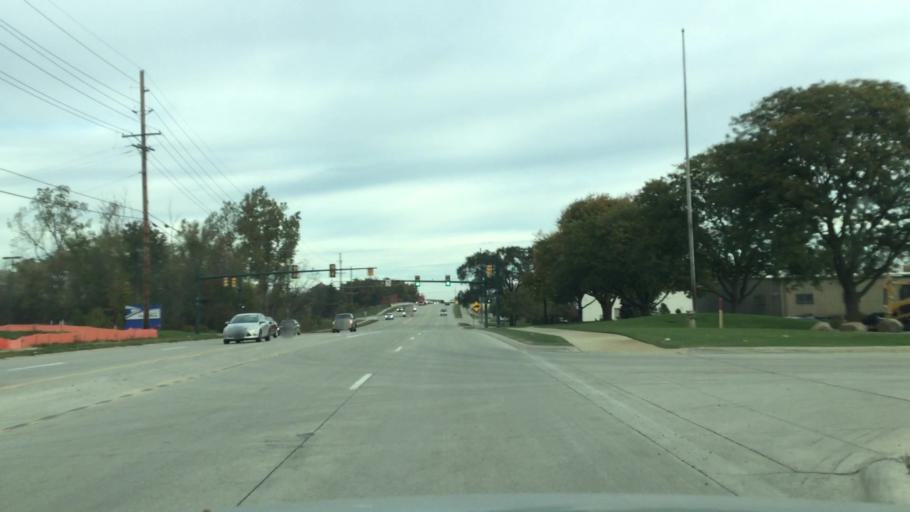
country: US
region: Michigan
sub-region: Oakland County
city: Novi
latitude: 42.4717
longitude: -83.4749
